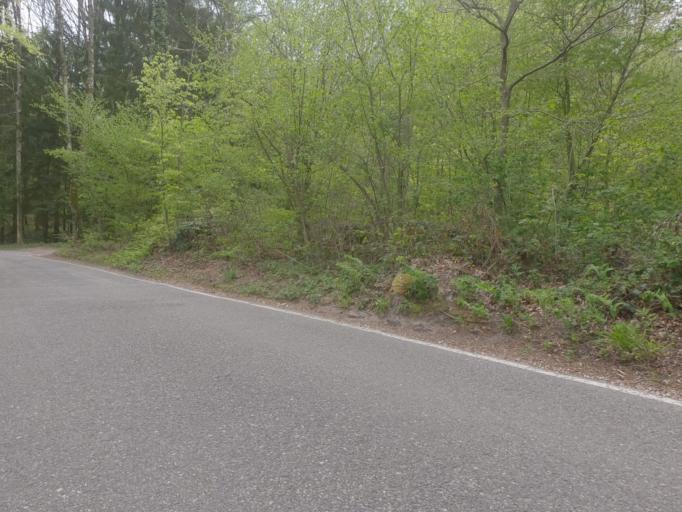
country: CH
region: Solothurn
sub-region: Bezirk Lebern
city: Riedholz
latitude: 47.2317
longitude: 7.5537
